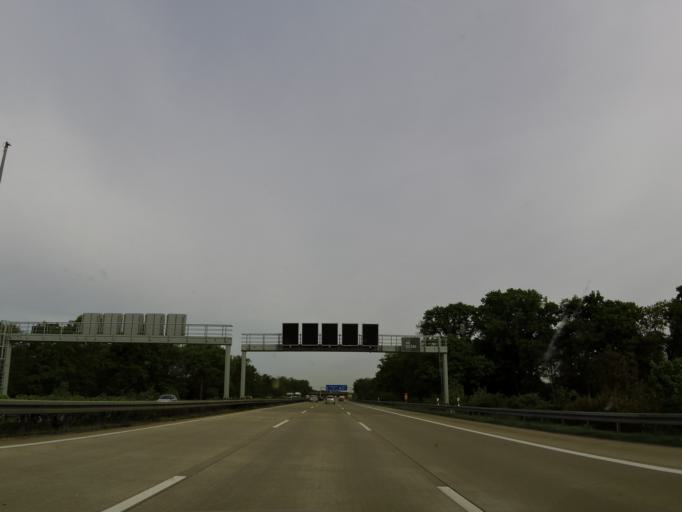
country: DE
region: Lower Saxony
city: Isernhagen Farster Bauerschaft
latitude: 52.5375
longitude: 9.8040
